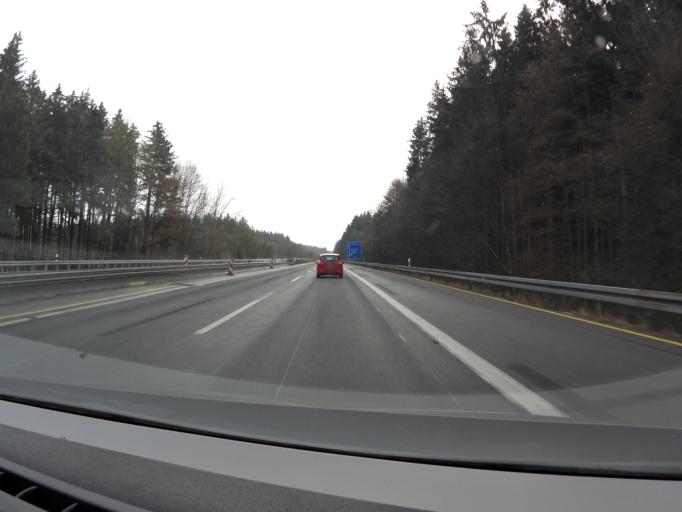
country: DE
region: Bavaria
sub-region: Upper Bavaria
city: Schaftlarn
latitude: 48.0049
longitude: 11.4215
